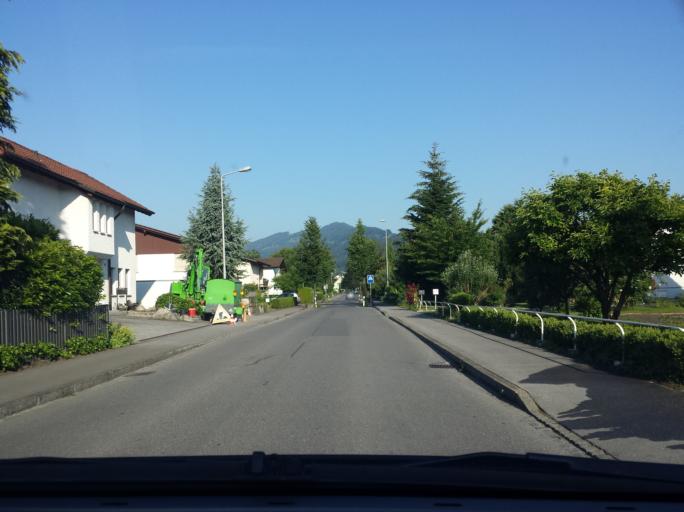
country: AT
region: Vorarlberg
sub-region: Politischer Bezirk Dornbirn
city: Lustenau
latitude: 47.4087
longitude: 9.6427
